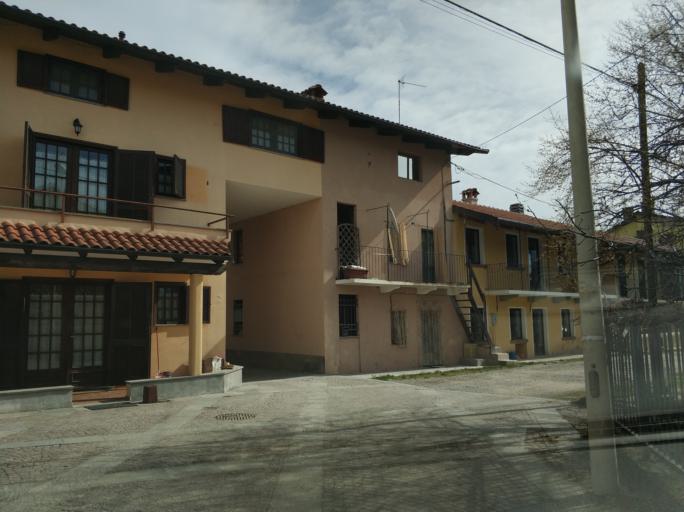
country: IT
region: Piedmont
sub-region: Provincia di Torino
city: Robassomero
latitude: 45.1998
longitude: 7.5906
